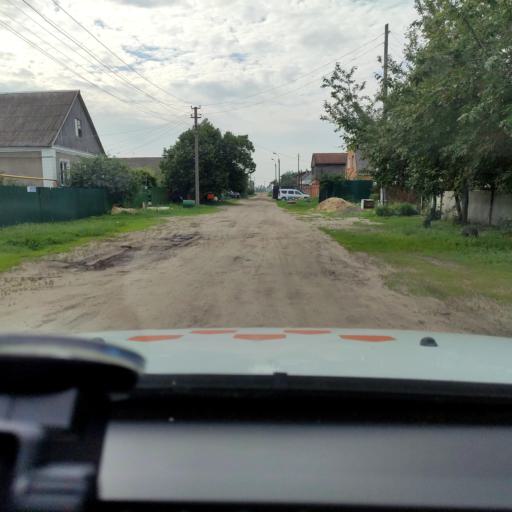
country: RU
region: Voronezj
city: Maslovka
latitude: 51.5810
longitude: 39.3069
